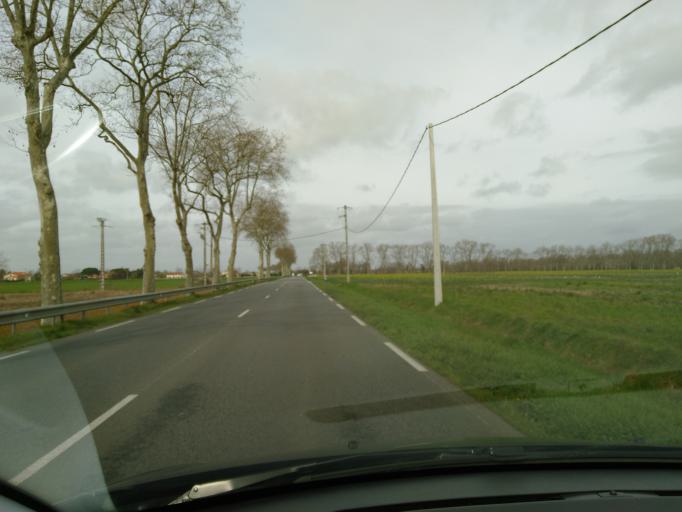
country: FR
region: Midi-Pyrenees
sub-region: Departement de la Haute-Garonne
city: Seilh
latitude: 43.7024
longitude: 1.3459
